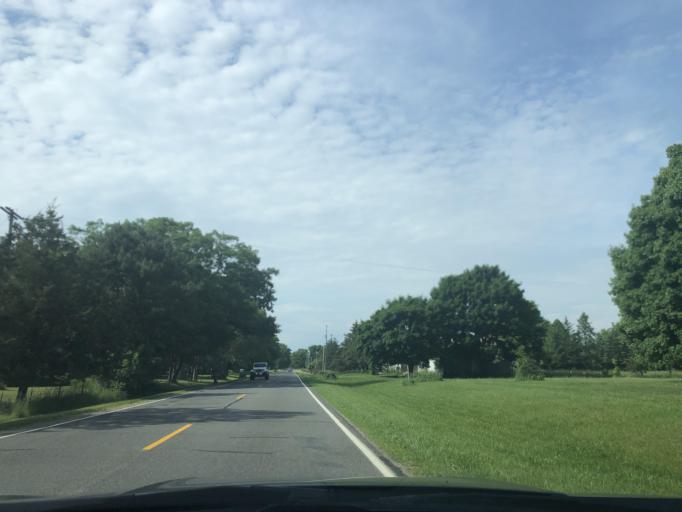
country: US
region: Michigan
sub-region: Clinton County
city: Bath
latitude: 42.8516
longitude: -84.4839
